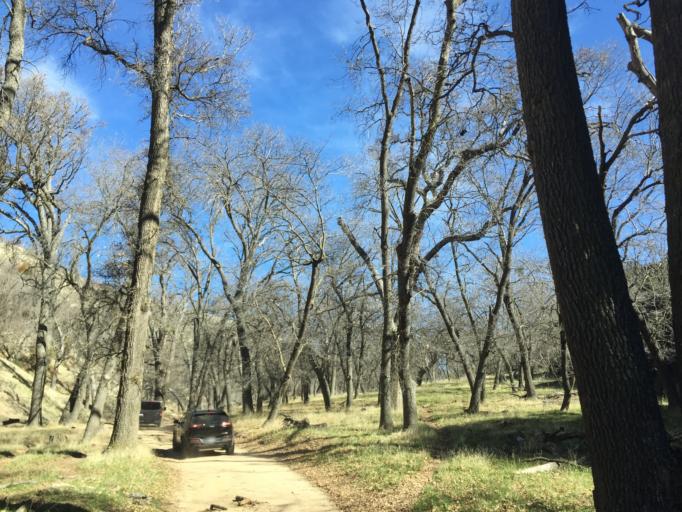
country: US
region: California
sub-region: Kern County
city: Lebec
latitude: 34.8918
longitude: -118.7451
